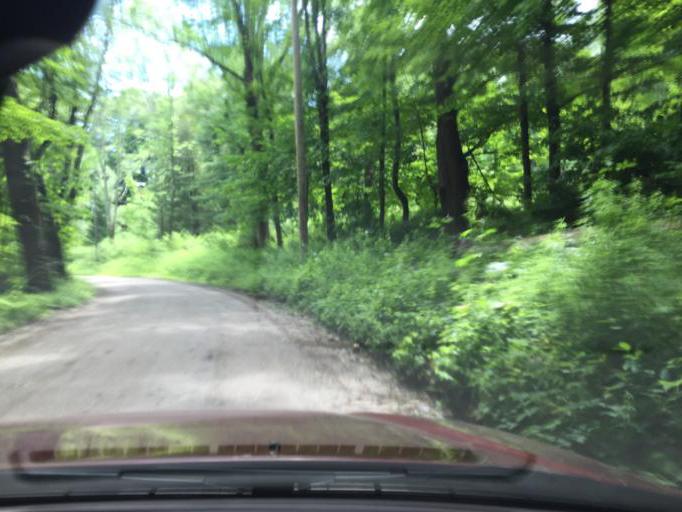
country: US
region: Connecticut
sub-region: Litchfield County
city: Litchfield
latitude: 41.7501
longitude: -73.2242
